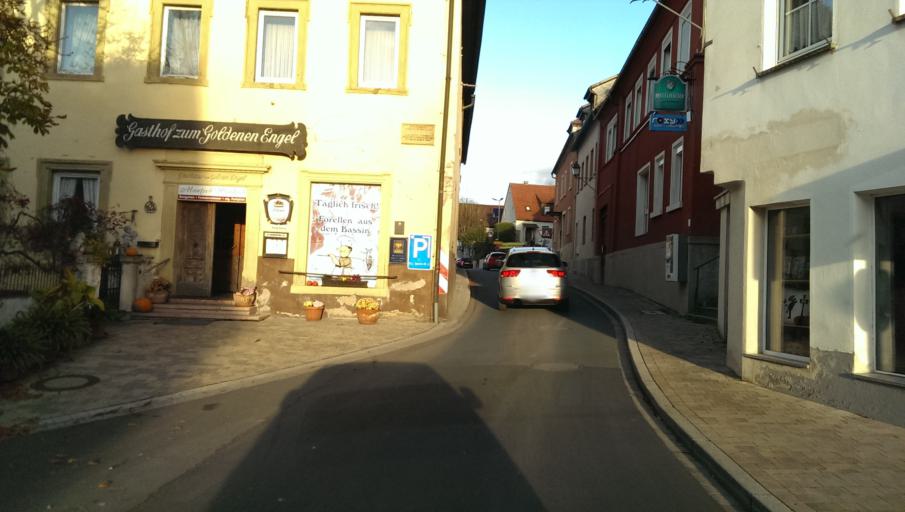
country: DE
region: Bavaria
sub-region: Regierungsbezirk Unterfranken
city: Arnstein
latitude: 49.9788
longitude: 9.9691
